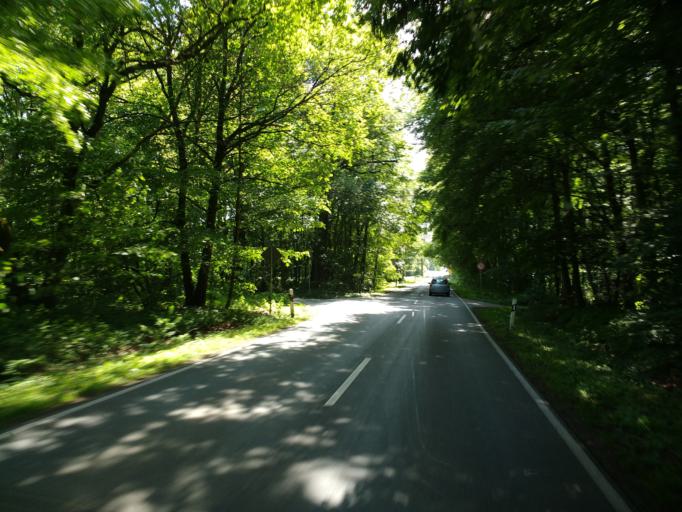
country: DE
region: Lower Saxony
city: Belm
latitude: 52.3110
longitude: 8.1081
